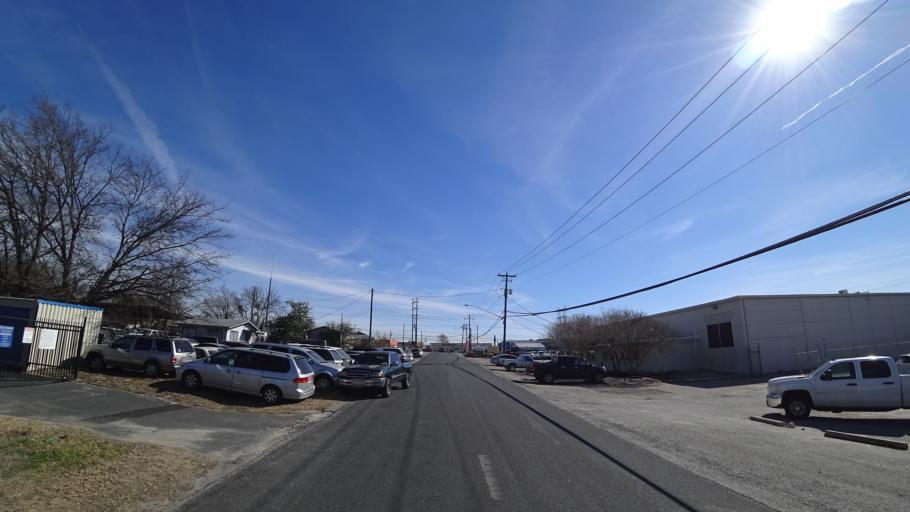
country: US
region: Texas
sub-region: Travis County
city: Wells Branch
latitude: 30.3781
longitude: -97.6905
